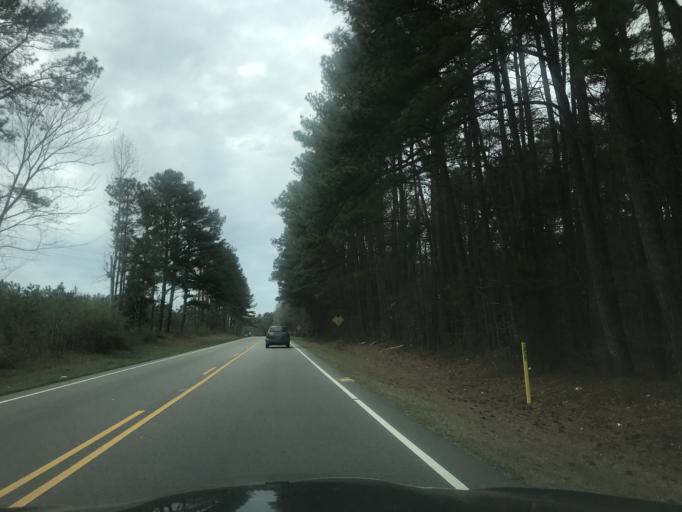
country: US
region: North Carolina
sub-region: Franklin County
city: Franklinton
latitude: 36.0996
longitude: -78.4253
